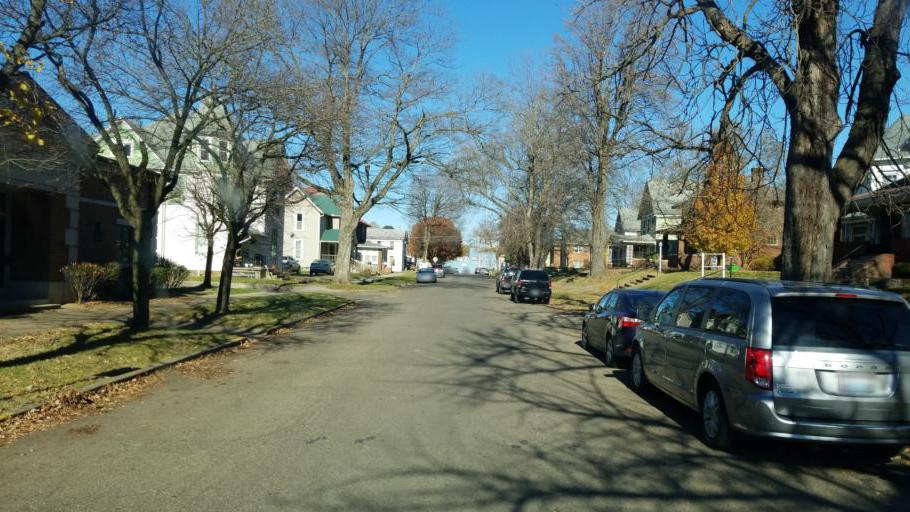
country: US
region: Ohio
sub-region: Coshocton County
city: Coshocton
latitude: 40.2753
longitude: -81.8651
